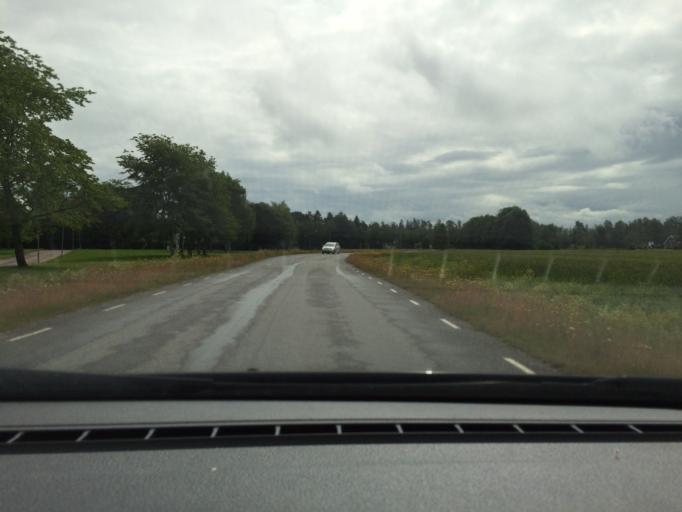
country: SE
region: Joenkoeping
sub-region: Varnamo Kommun
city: Forsheda
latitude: 57.1574
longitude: 13.8215
